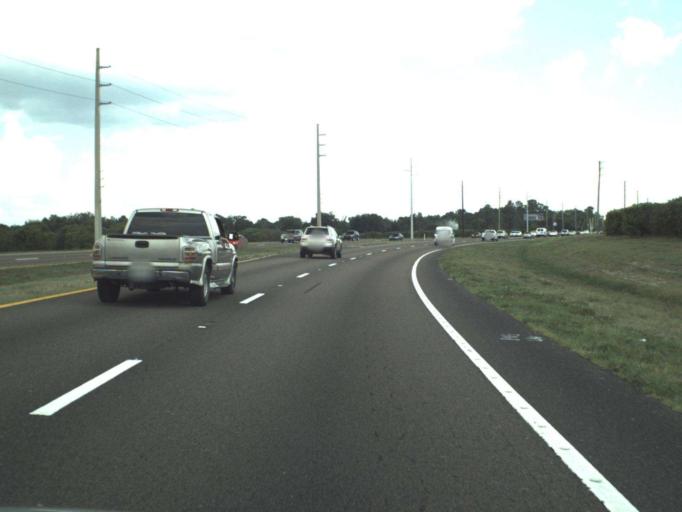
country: US
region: Florida
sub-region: Lake County
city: Mount Dora
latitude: 28.8233
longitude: -81.6371
